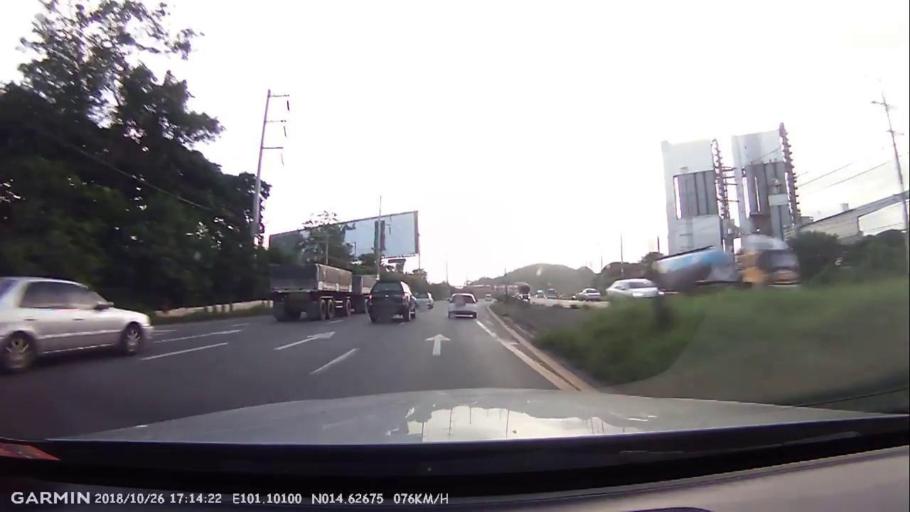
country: TH
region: Sara Buri
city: Muak Lek
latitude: 14.6261
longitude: 101.1010
